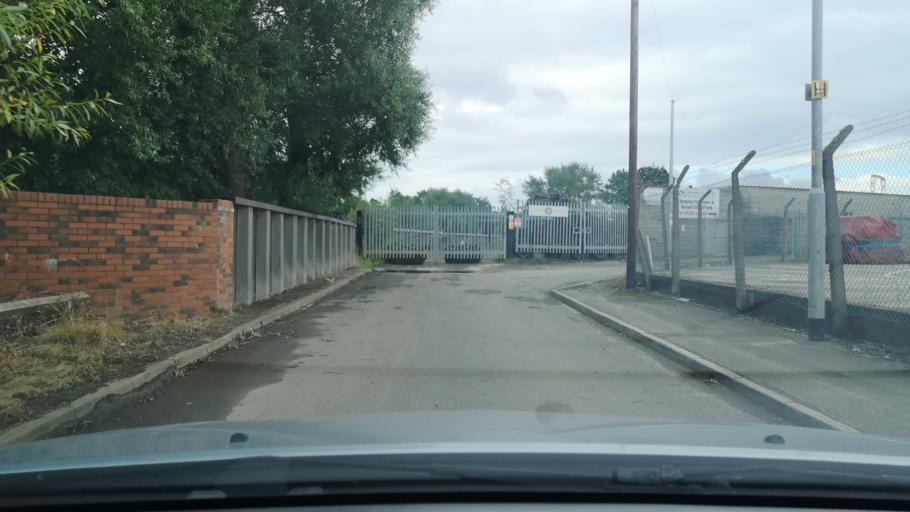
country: GB
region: England
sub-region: City and Borough of Wakefield
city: Wakefield
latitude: 53.6703
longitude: -1.4922
